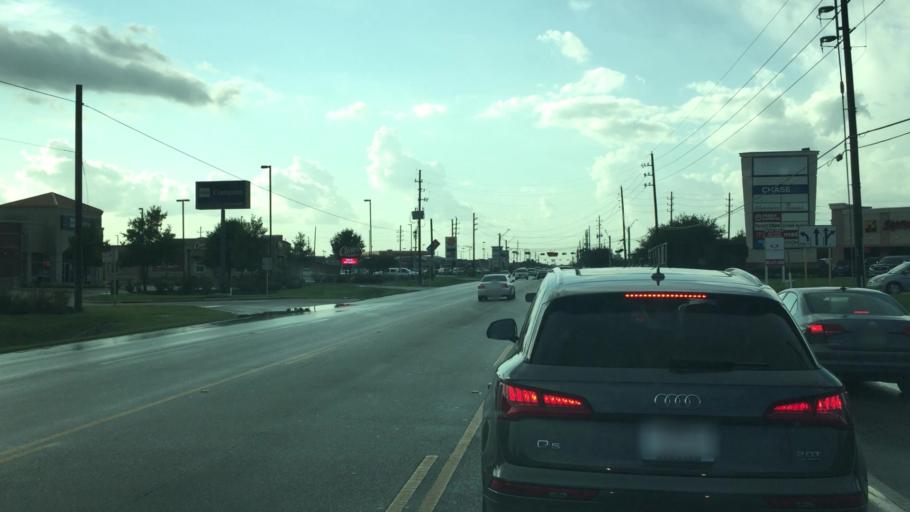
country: US
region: Texas
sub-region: Montgomery County
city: The Woodlands
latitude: 30.0725
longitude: -95.5117
